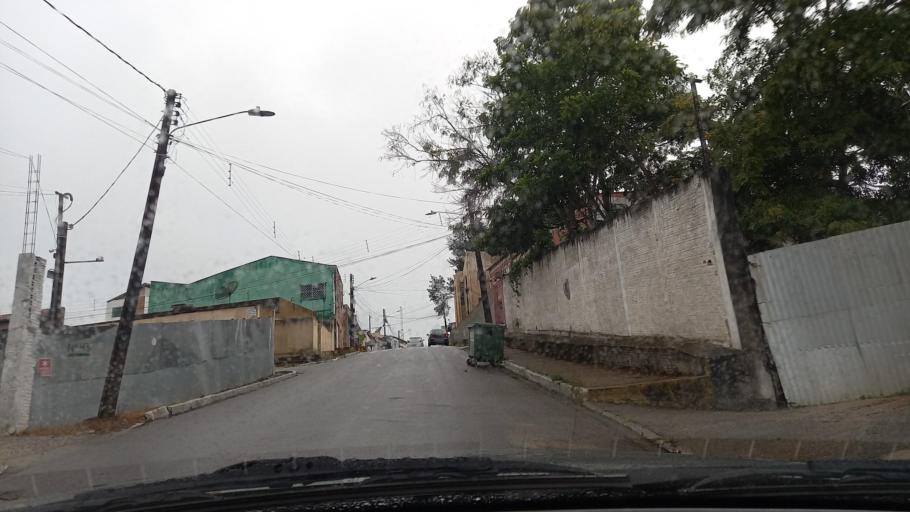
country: BR
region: Pernambuco
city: Garanhuns
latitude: -8.8846
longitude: -36.4970
